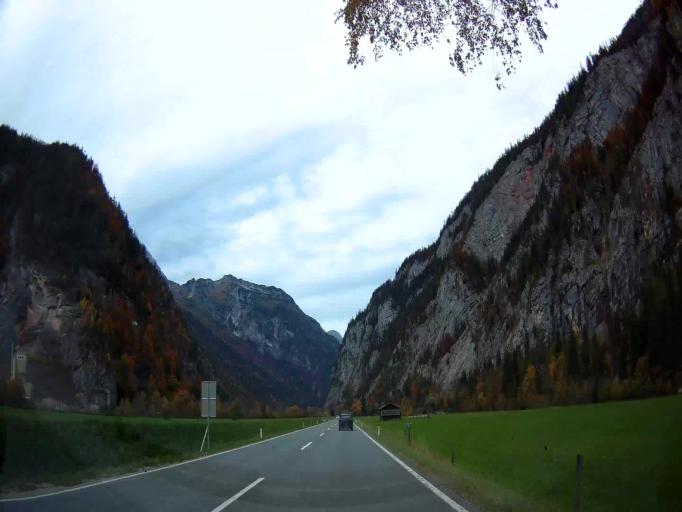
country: AT
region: Salzburg
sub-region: Politischer Bezirk Zell am See
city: Leogang
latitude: 47.4993
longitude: 12.7914
